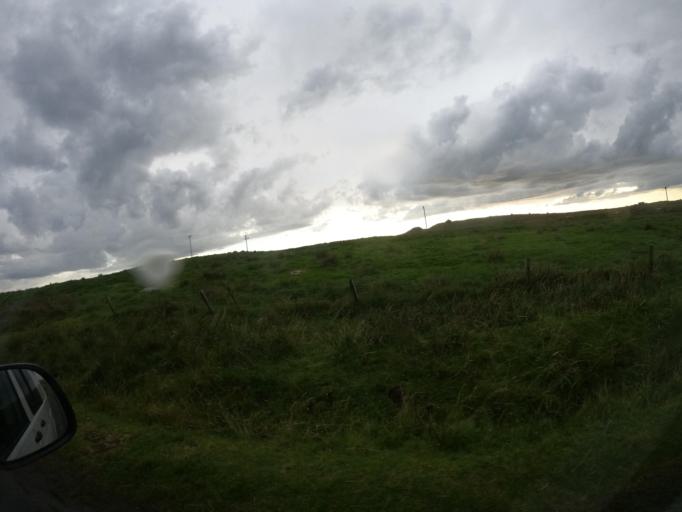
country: GB
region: Scotland
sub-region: Eilean Siar
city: Barra
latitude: 56.5101
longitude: -6.8114
